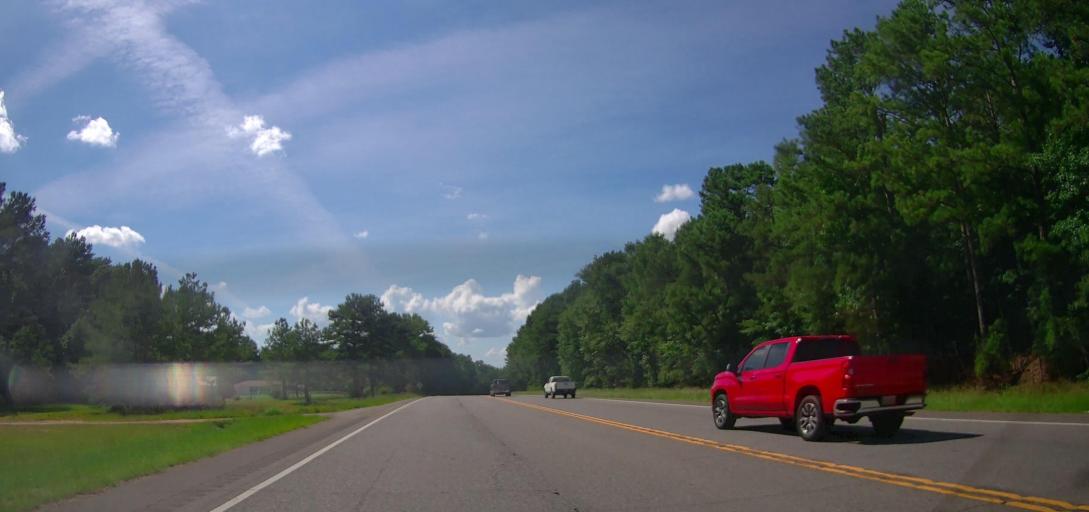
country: US
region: Alabama
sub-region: Pickens County
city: Gordo
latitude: 33.2897
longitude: -87.8690
